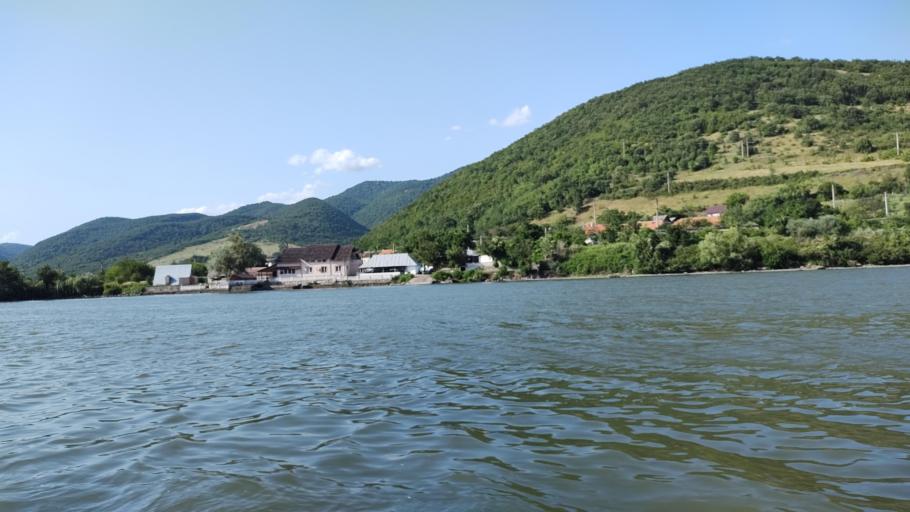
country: RO
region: Caras-Severin
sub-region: Comuna Berzasca
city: Berzasca
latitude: 44.6383
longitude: 21.9531
